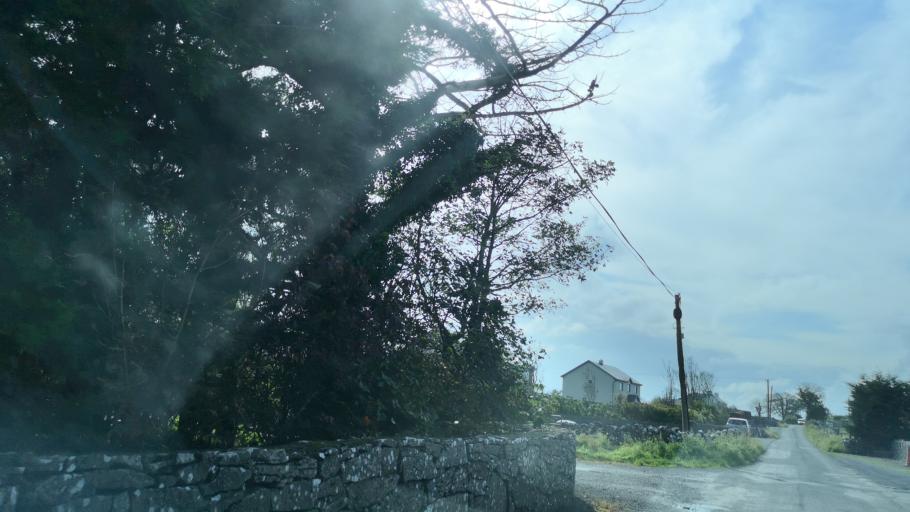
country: IE
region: Connaught
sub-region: County Galway
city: Athenry
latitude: 53.3069
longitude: -8.8101
